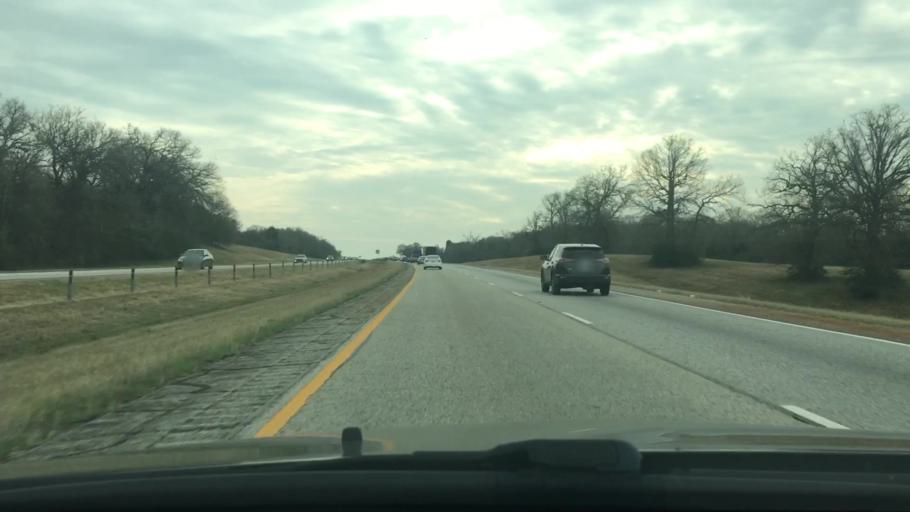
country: US
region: Texas
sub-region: Leon County
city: Centerville
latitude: 31.2334
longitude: -95.9941
